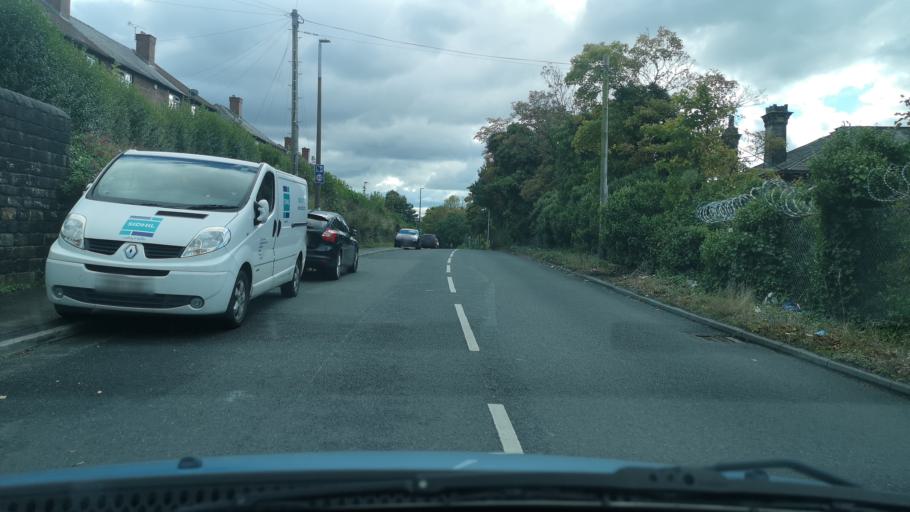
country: GB
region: England
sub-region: Kirklees
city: Heckmondwike
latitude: 53.6995
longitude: -1.6613
